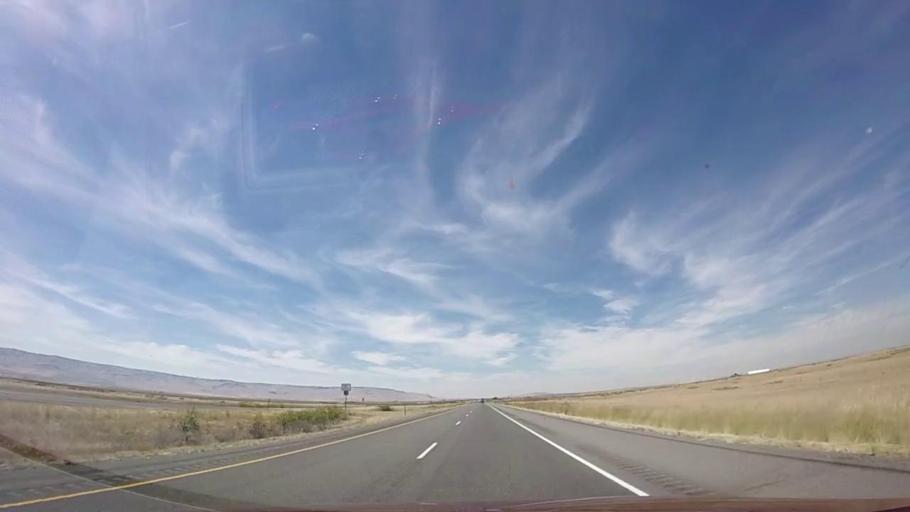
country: US
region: Idaho
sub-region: Minidoka County
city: Rupert
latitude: 42.4090
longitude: -113.3117
